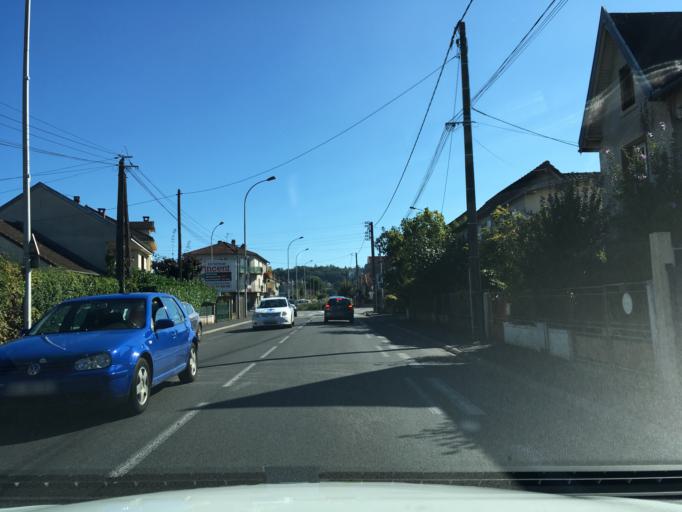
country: FR
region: Limousin
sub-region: Departement de la Correze
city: Brive-la-Gaillarde
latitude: 45.1572
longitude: 1.5040
